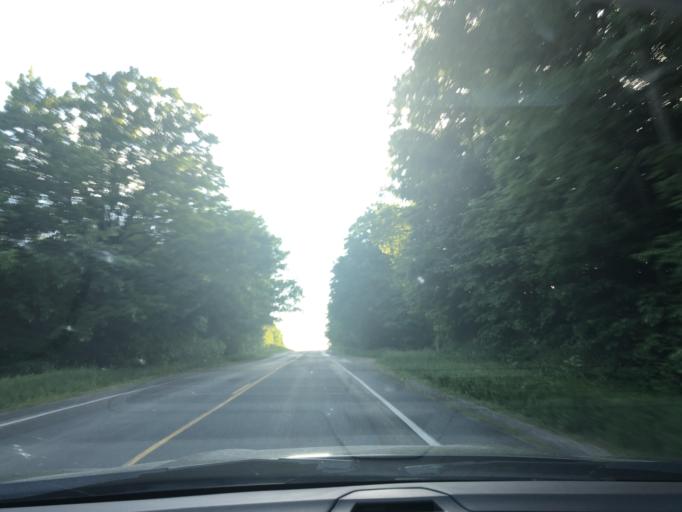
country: US
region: Michigan
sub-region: Missaukee County
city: Lake City
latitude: 44.4669
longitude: -85.1065
